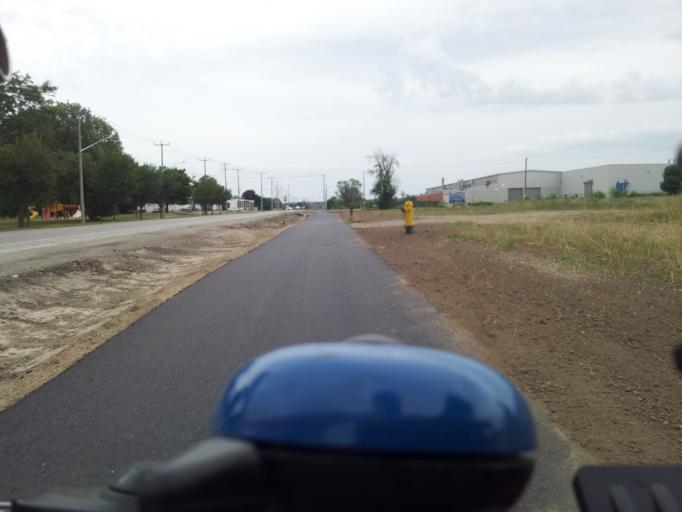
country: CA
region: Ontario
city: Stratford
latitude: 43.3592
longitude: -81.0038
